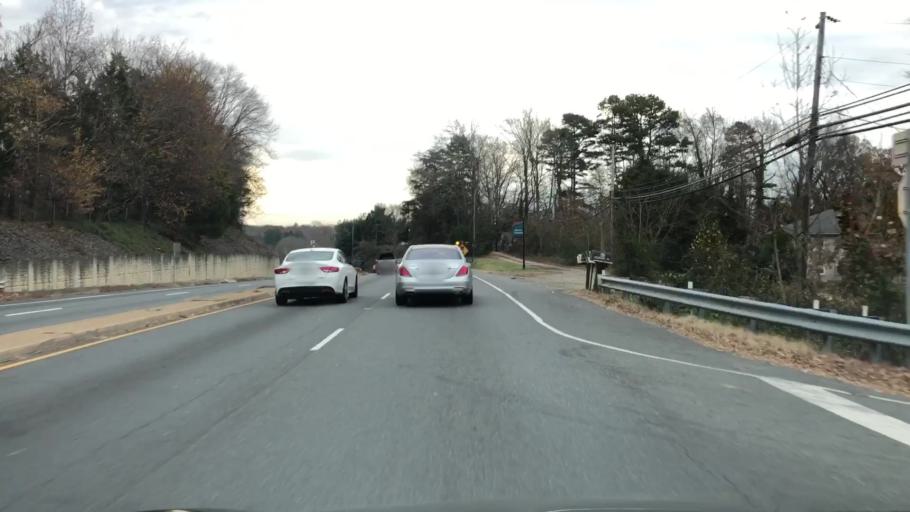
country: US
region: Virginia
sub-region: Stafford County
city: Falmouth
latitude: 38.3263
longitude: -77.4727
